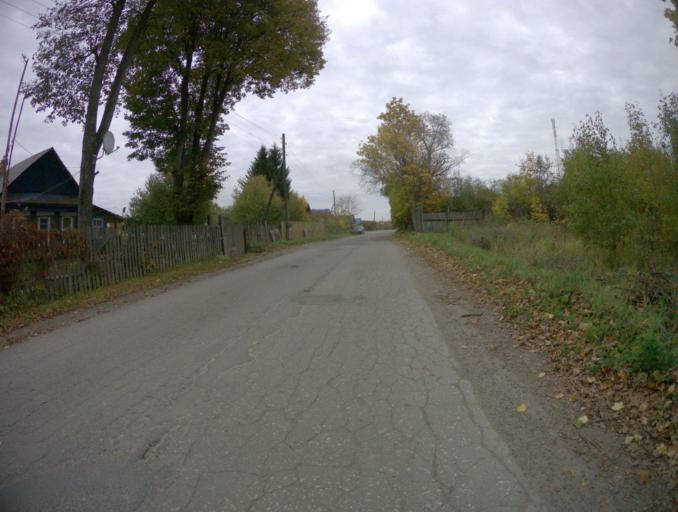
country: RU
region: Vladimir
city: Stepantsevo
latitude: 56.3149
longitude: 41.6303
